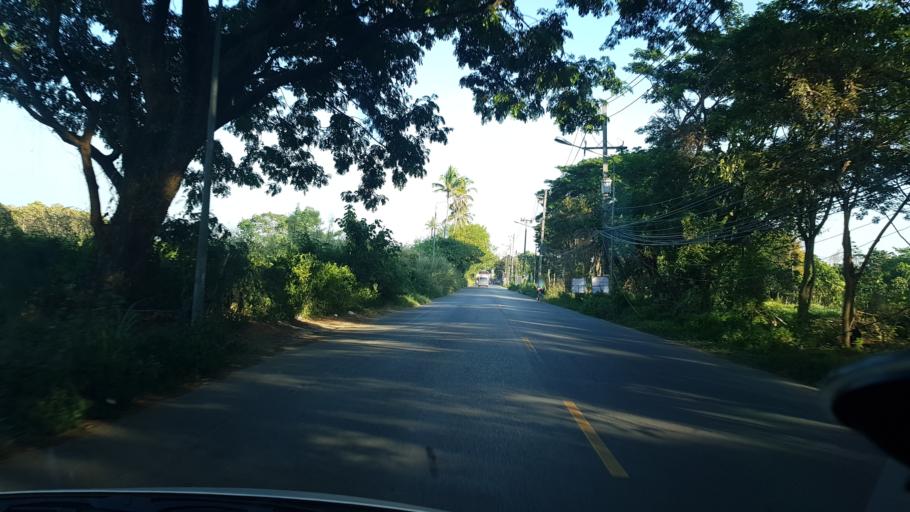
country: TH
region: Chiang Rai
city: Chiang Rai
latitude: 19.9300
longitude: 99.8258
